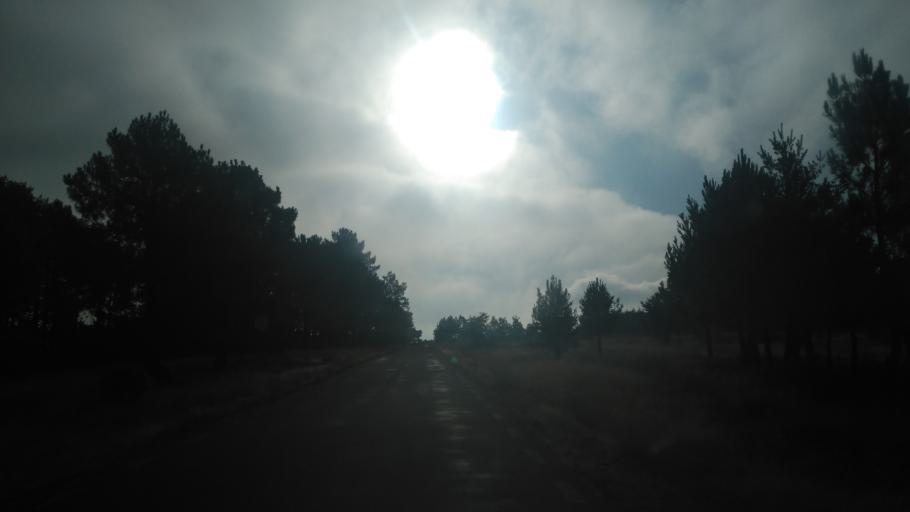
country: ES
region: Castille and Leon
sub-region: Provincia de Salamanca
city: Nava de Francia
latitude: 40.5235
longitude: -6.1140
